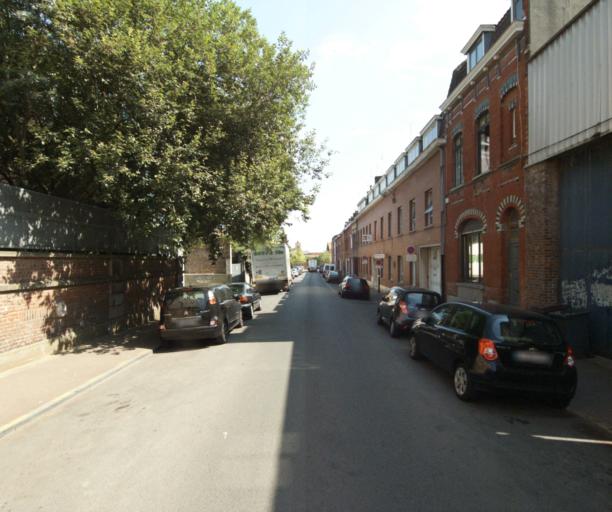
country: FR
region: Nord-Pas-de-Calais
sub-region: Departement du Nord
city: Tourcoing
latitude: 50.7259
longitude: 3.1594
